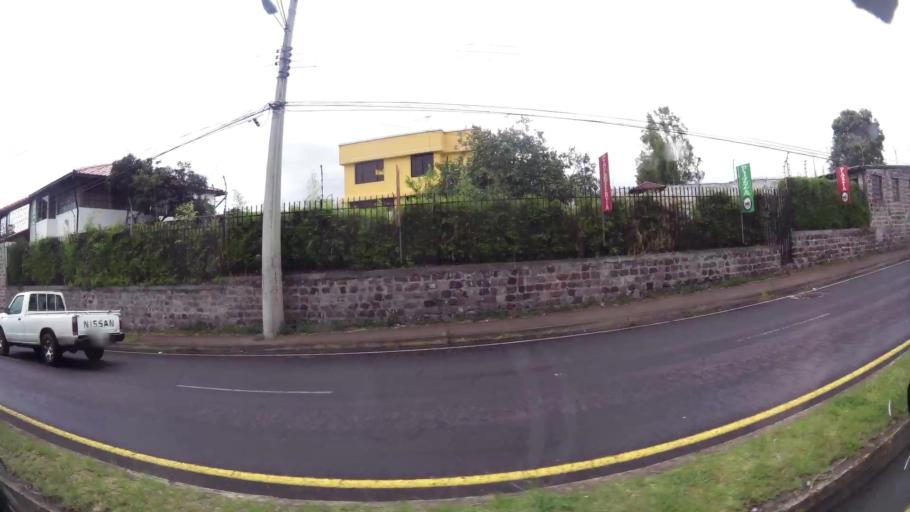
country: EC
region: Pichincha
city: Sangolqui
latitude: -0.3227
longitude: -78.4413
